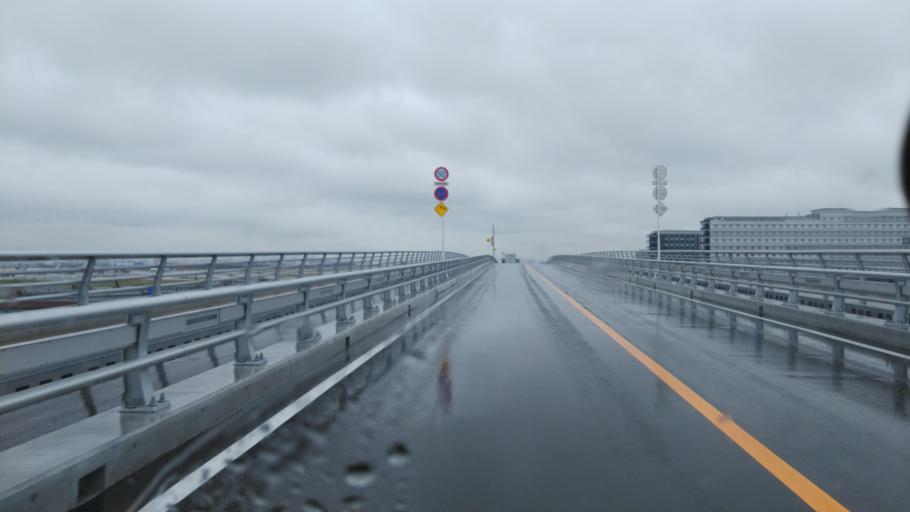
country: JP
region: Kanagawa
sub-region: Kawasaki-shi
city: Kawasaki
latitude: 35.5418
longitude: 139.7618
